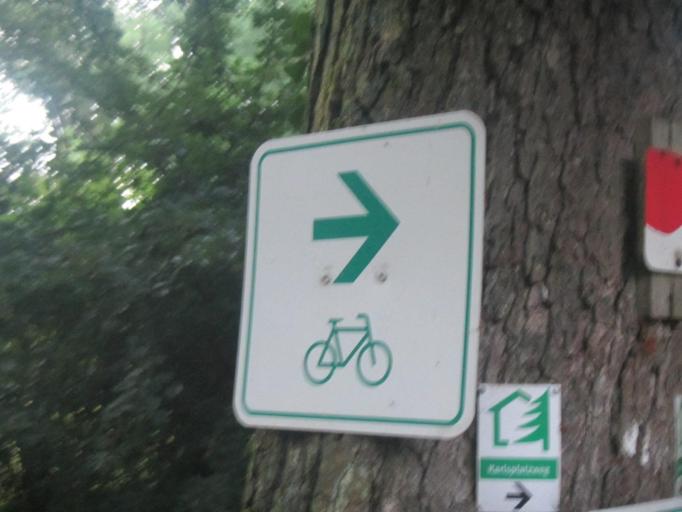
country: DE
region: Rheinland-Pfalz
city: Klingenmunster
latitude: 49.1384
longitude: 8.0079
